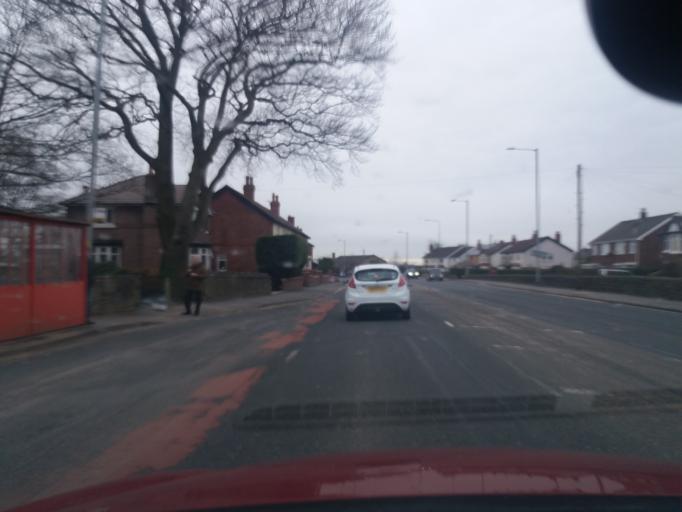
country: GB
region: England
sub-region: Lancashire
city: Chorley
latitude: 53.6642
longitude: -2.6322
